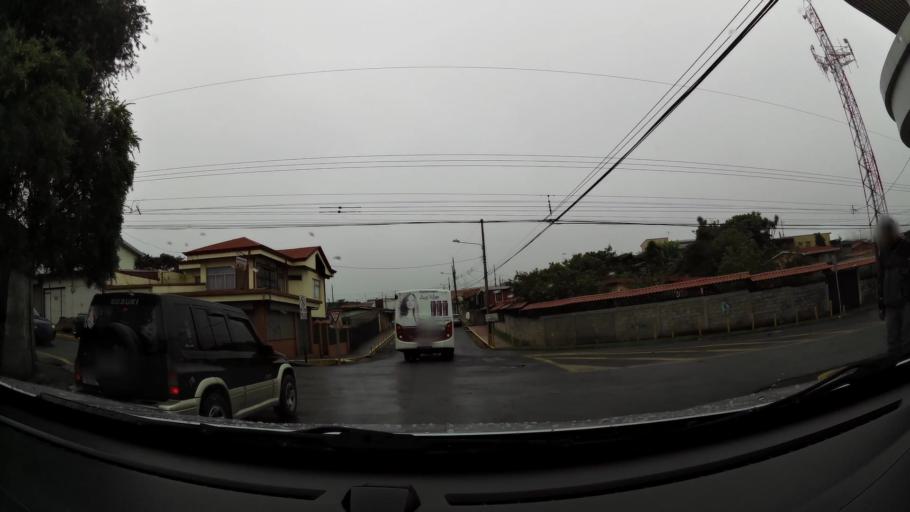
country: CR
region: Cartago
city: Paraiso
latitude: 9.8400
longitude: -83.8654
